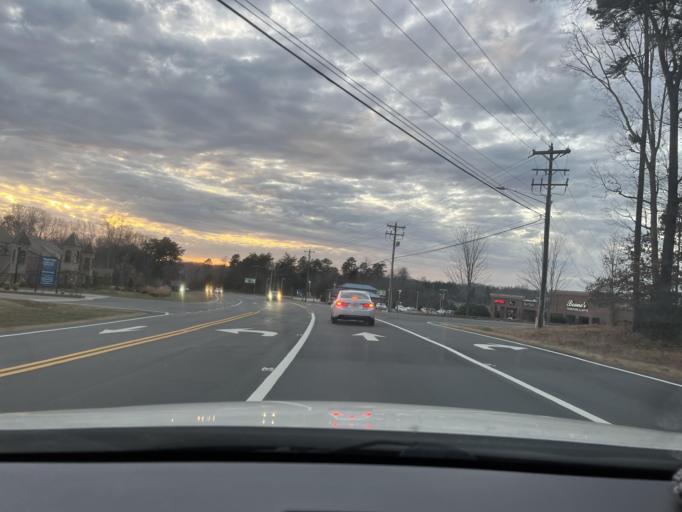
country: US
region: North Carolina
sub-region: Guilford County
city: Gibsonville
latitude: 36.0812
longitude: -79.5386
